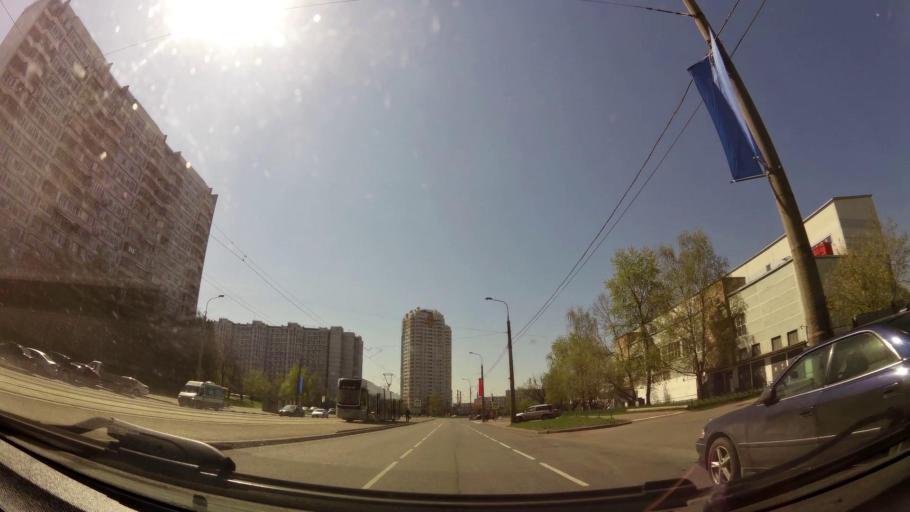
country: RU
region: Moscow
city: Strogino
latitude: 55.8019
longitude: 37.3914
